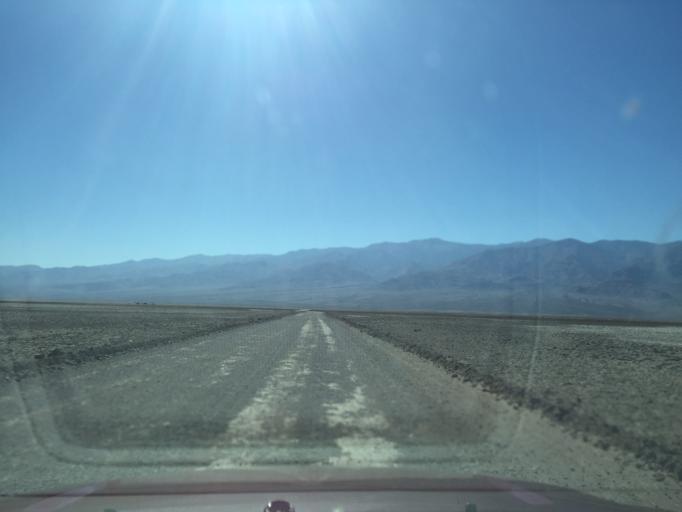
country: US
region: Nevada
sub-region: Nye County
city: Beatty
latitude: 36.2920
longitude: -116.8212
